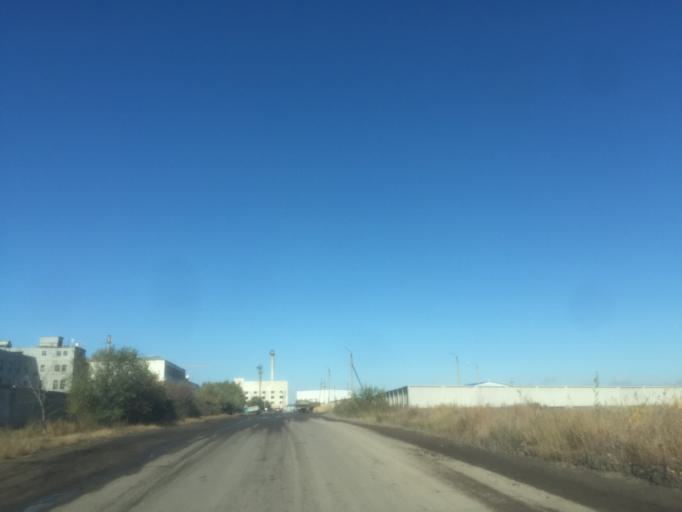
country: KZ
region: Astana Qalasy
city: Astana
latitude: 51.2143
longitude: 71.3553
